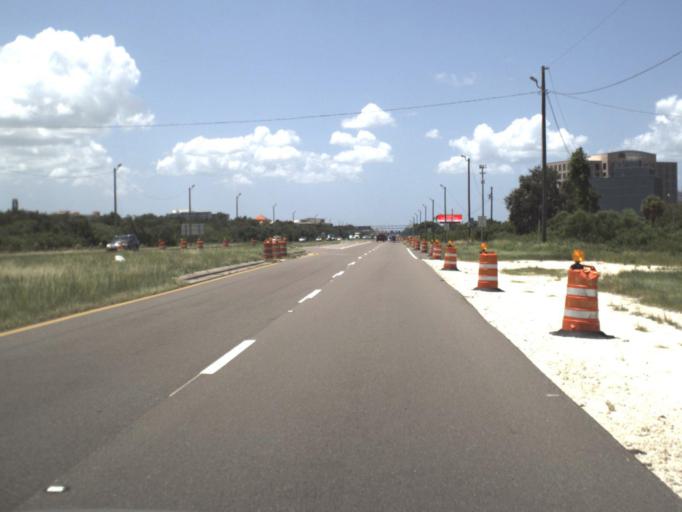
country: US
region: Florida
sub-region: Pinellas County
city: Feather Sound
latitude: 27.8939
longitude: -82.6540
